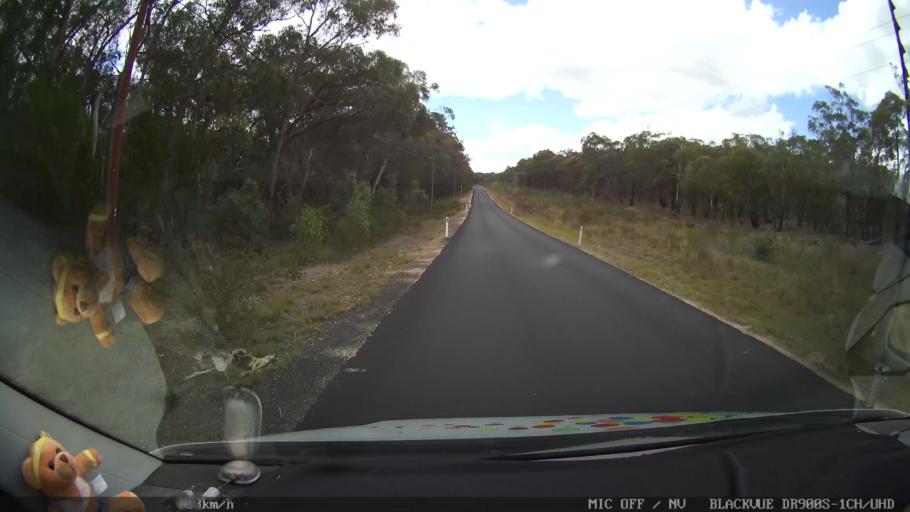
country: AU
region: New South Wales
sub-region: Glen Innes Severn
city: Glen Innes
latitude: -29.4400
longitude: 151.6204
